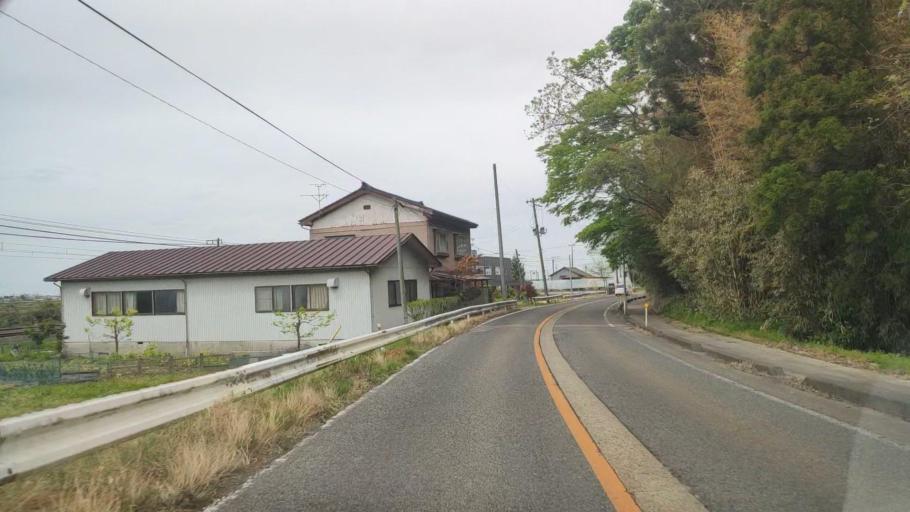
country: JP
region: Niigata
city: Shirone
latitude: 37.7307
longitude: 139.0816
